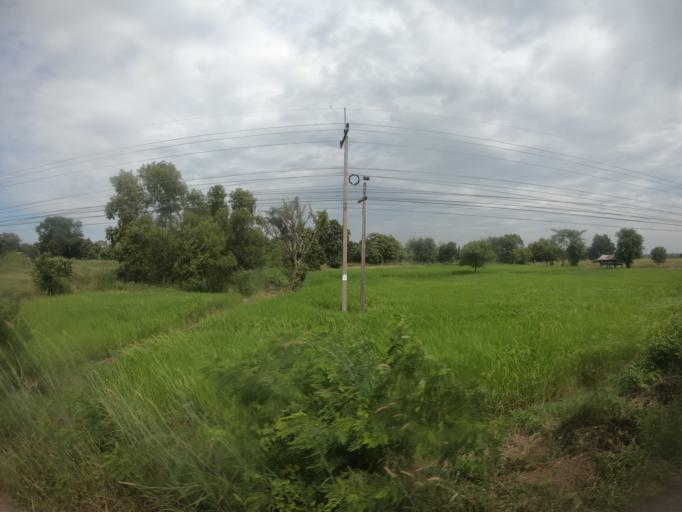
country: TH
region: Maha Sarakham
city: Chiang Yuen
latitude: 16.3397
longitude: 103.1597
